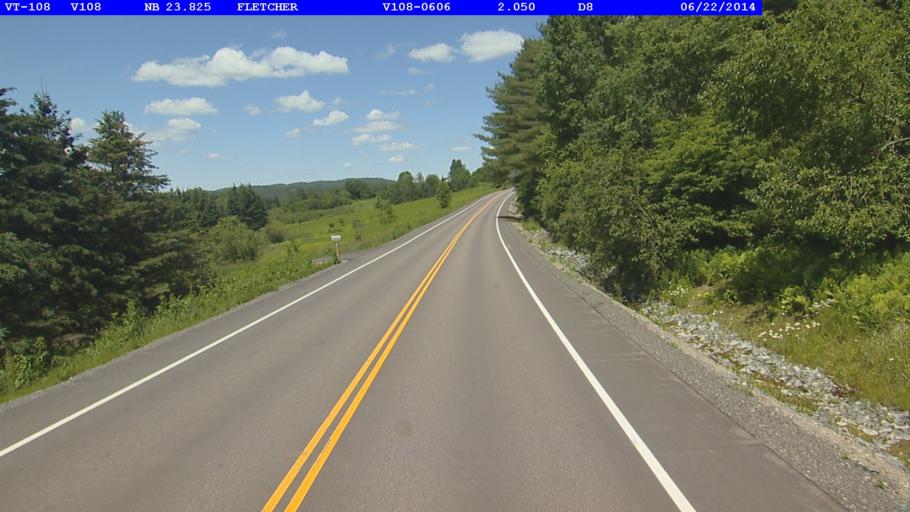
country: US
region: Vermont
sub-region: Lamoille County
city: Johnson
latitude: 44.7298
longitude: -72.8292
